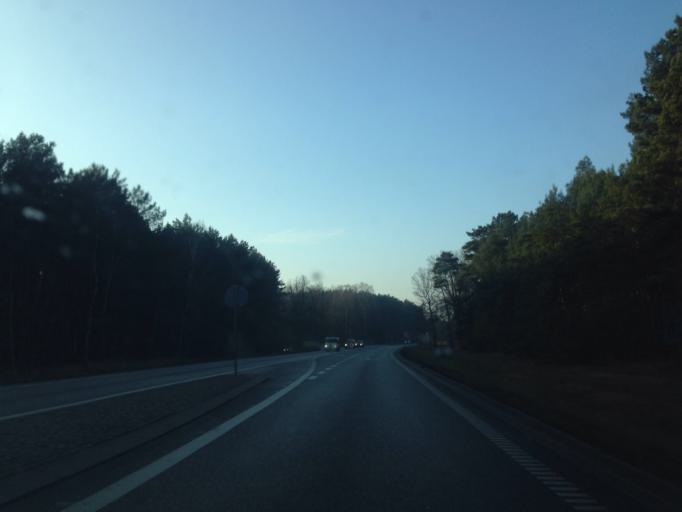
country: PL
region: Kujawsko-Pomorskie
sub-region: Powiat bydgoski
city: Solec Kujawski
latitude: 53.0610
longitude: 18.1874
